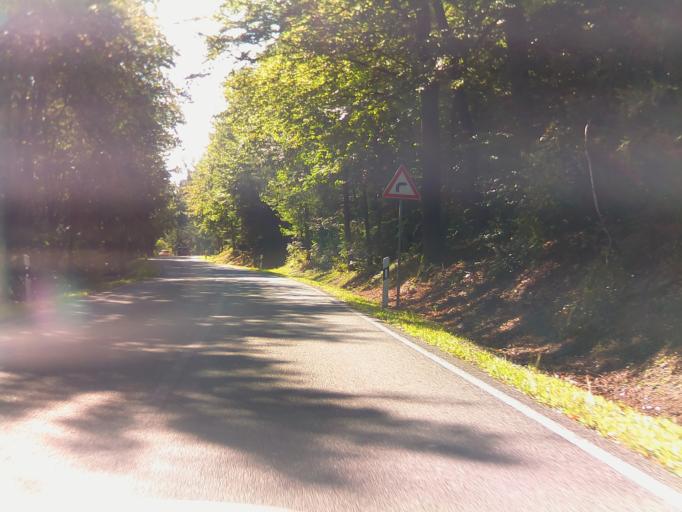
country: DE
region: Thuringia
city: Wurzbach
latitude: 50.4779
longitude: 11.4685
